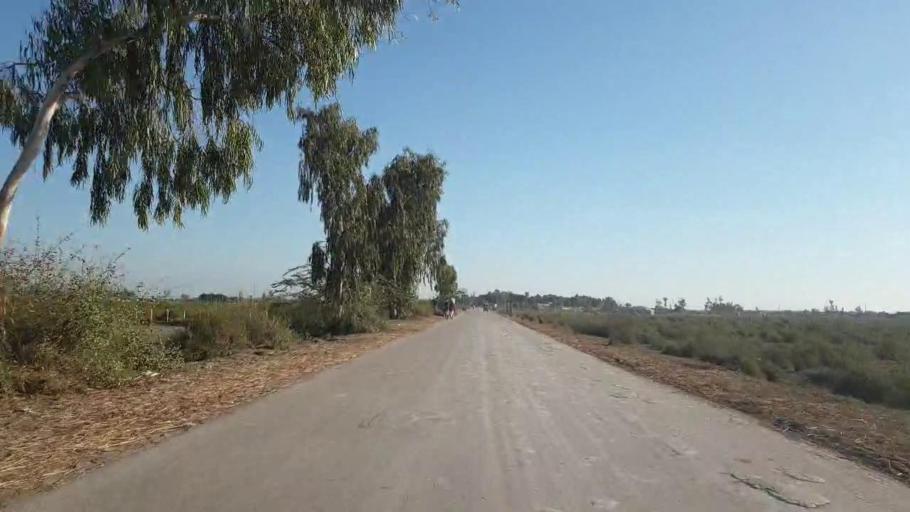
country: PK
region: Sindh
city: Dokri
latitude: 27.3355
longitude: 68.1284
